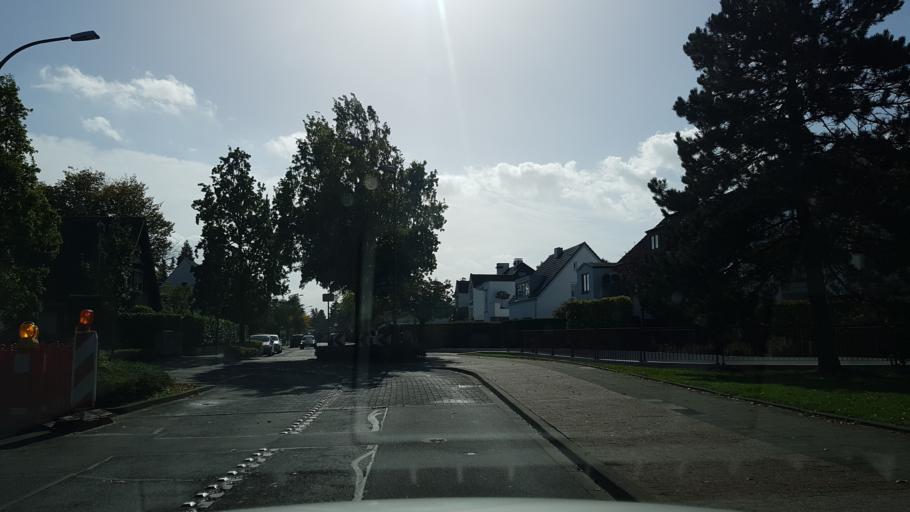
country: DE
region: North Rhine-Westphalia
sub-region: Regierungsbezirk Dusseldorf
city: Meerbusch
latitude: 51.2458
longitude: 6.6885
